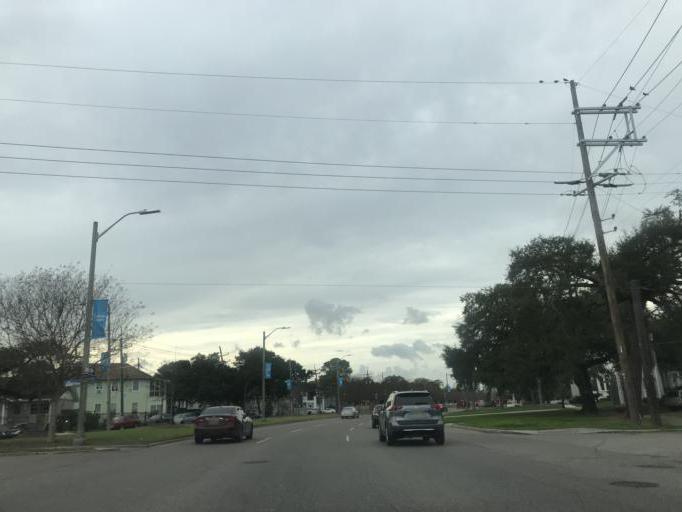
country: US
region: Louisiana
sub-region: Orleans Parish
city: New Orleans
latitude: 29.9401
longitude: -90.1070
